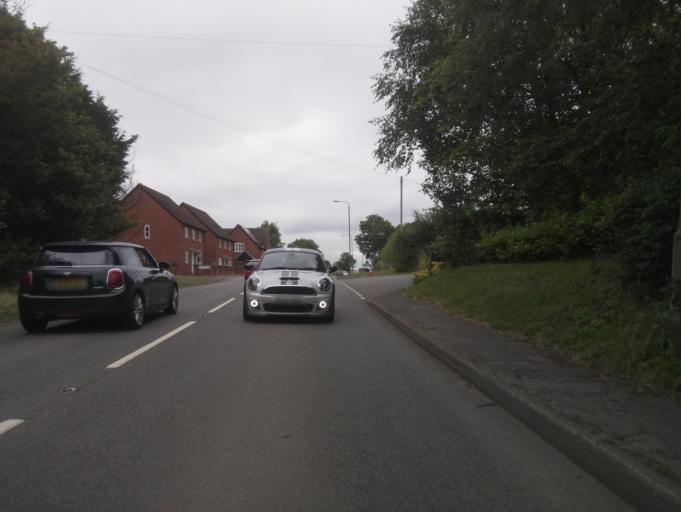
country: GB
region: England
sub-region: Nottinghamshire
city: East Leake
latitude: 52.8132
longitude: -1.1384
